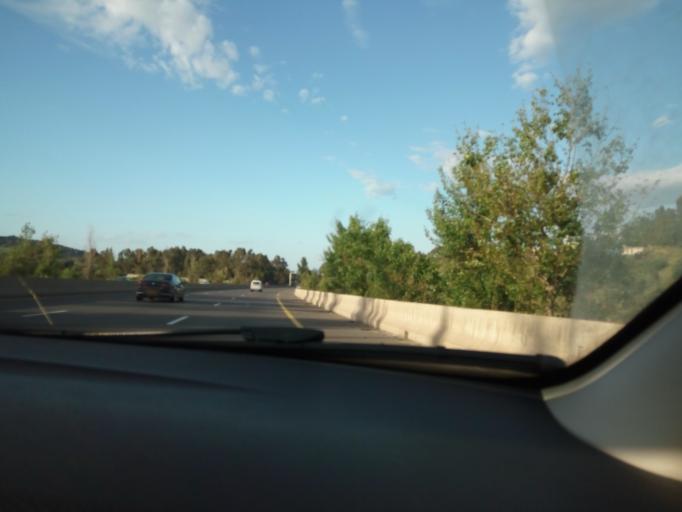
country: DZ
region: Tipaza
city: El Affroun
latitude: 36.4405
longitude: 2.5798
